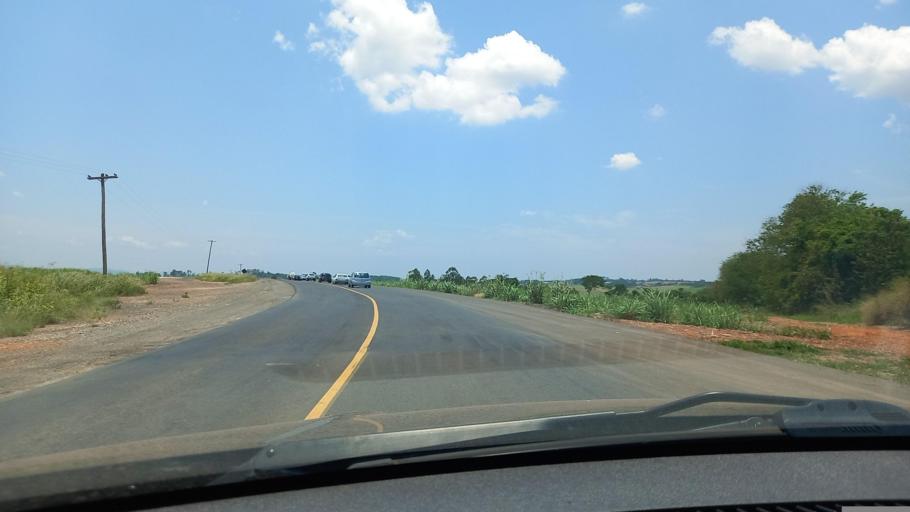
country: BR
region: Sao Paulo
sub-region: Itapira
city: Itapira
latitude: -22.3847
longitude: -46.8679
